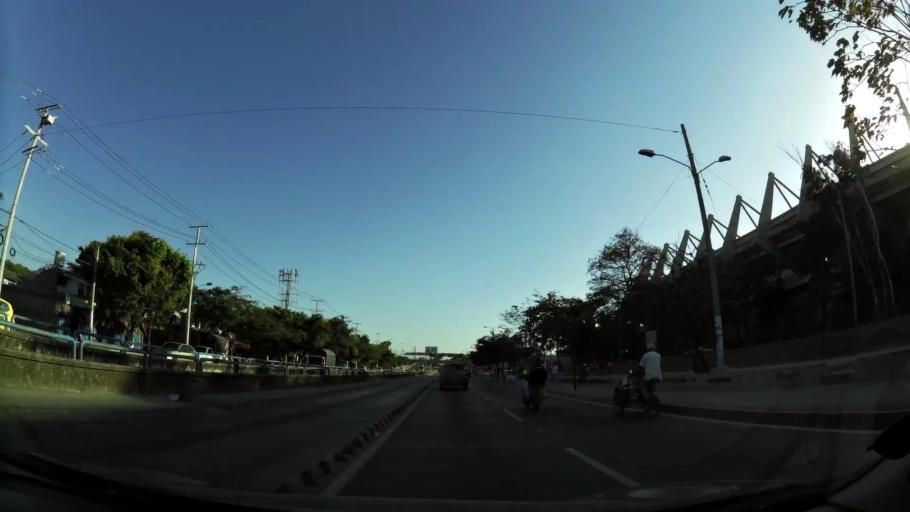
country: CO
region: Atlantico
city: Soledad
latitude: 10.9276
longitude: -74.7992
